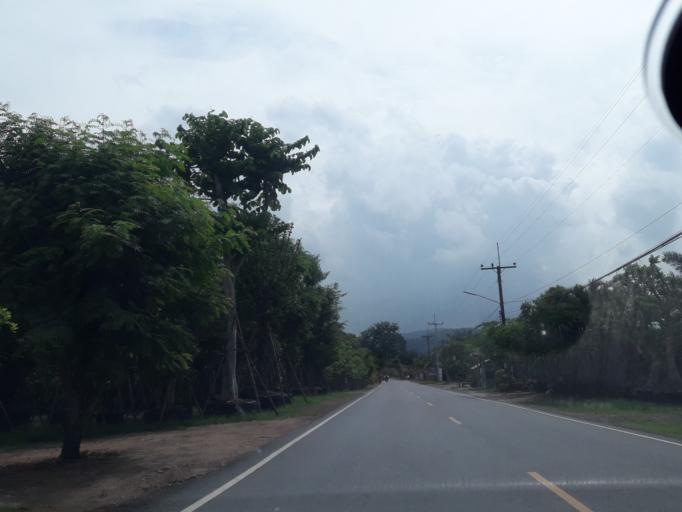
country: TH
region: Sara Buri
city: Wihan Daeng
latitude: 14.4202
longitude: 101.1241
